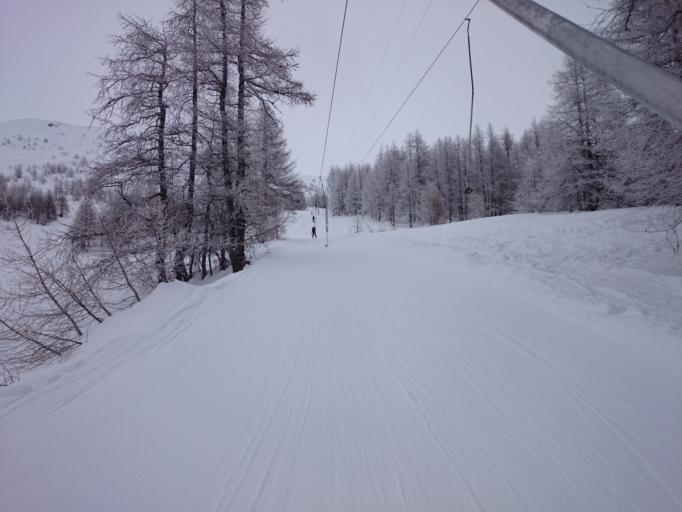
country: IT
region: Piedmont
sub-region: Provincia di Torino
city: Prali
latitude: 44.7916
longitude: 6.9541
